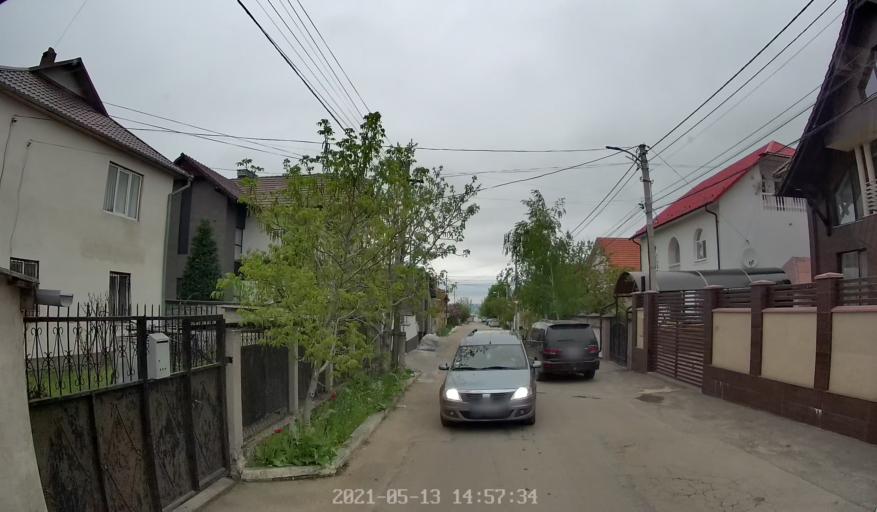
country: MD
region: Chisinau
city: Stauceni
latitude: 47.1011
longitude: 28.8712
